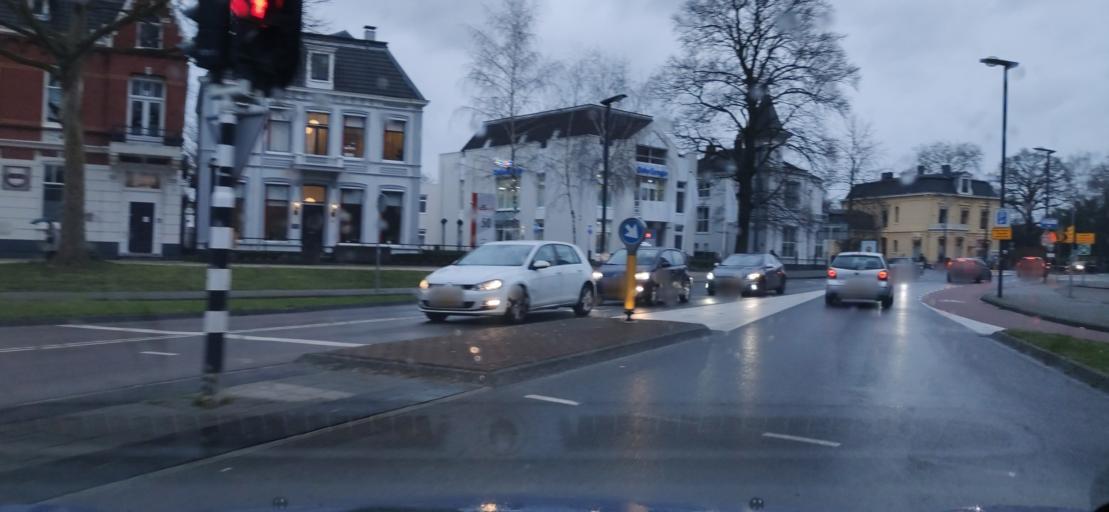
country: NL
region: Overijssel
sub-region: Gemeente Enschede
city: Enschede
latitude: 52.2234
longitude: 6.8876
